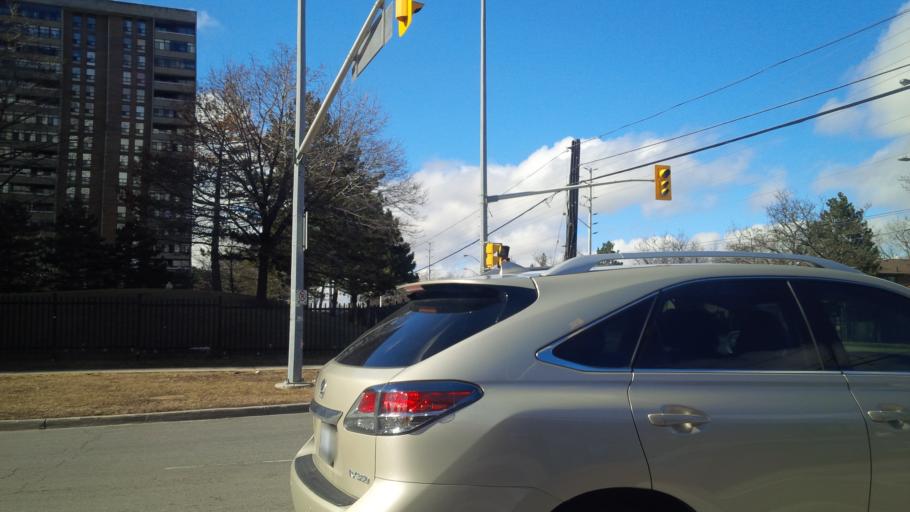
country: CA
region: Ontario
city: Brampton
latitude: 43.7214
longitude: -79.7141
